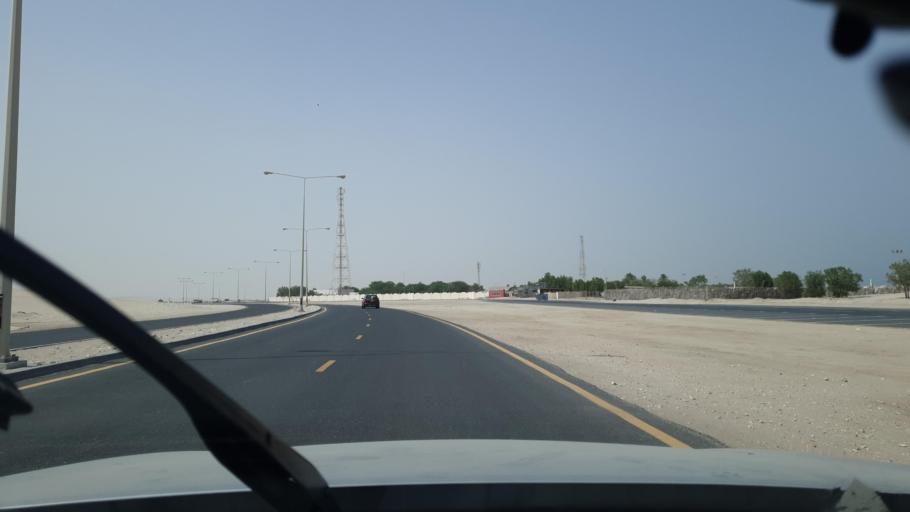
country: QA
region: Al Wakrah
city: Umm Sa'id
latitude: 24.8556
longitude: 51.5105
